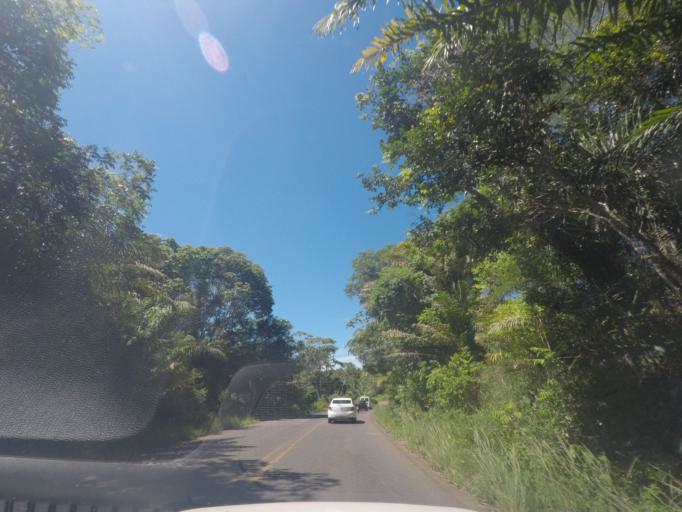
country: BR
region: Bahia
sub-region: Taperoa
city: Taperoa
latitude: -13.4615
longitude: -39.0892
